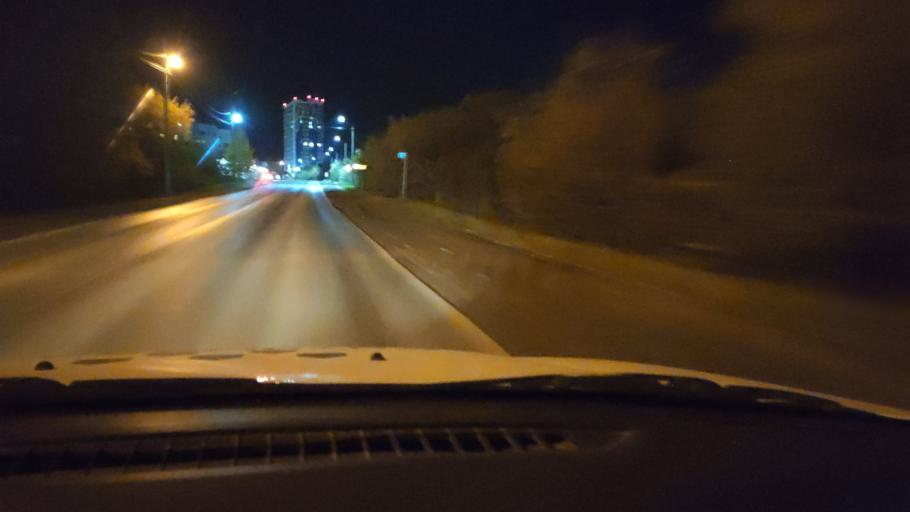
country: RU
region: Perm
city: Kondratovo
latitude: 57.9731
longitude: 56.1121
